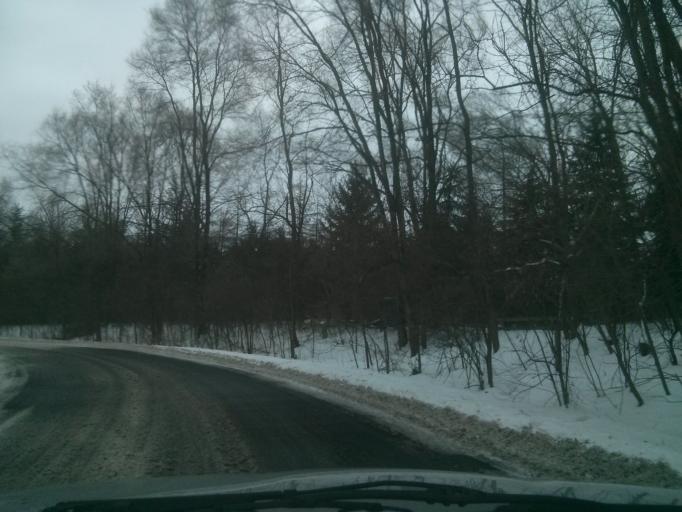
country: US
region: Minnesota
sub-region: Washington County
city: Lake Saint Croix Beach
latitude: 44.9357
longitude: -92.7743
